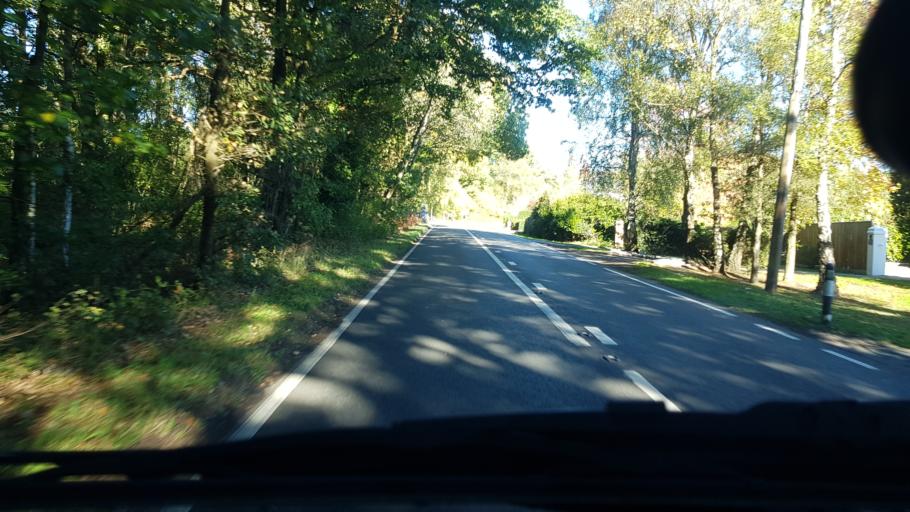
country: GB
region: England
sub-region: Surrey
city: Pirbright
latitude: 51.2794
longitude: -0.6486
